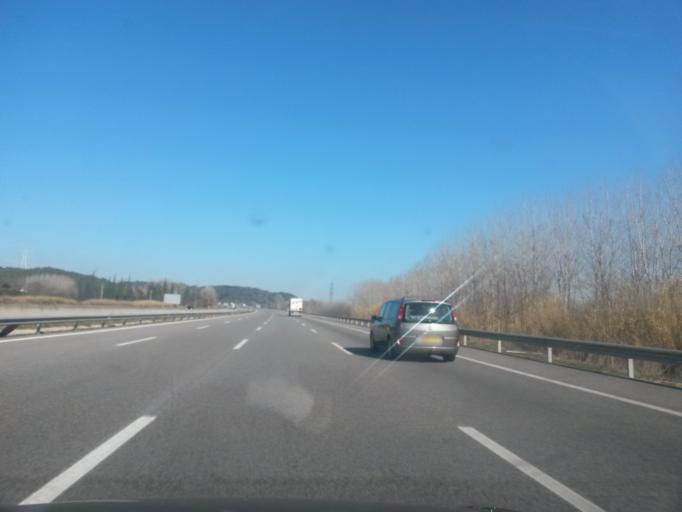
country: ES
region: Catalonia
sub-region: Provincia de Girona
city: Celra
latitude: 42.0480
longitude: 2.8715
